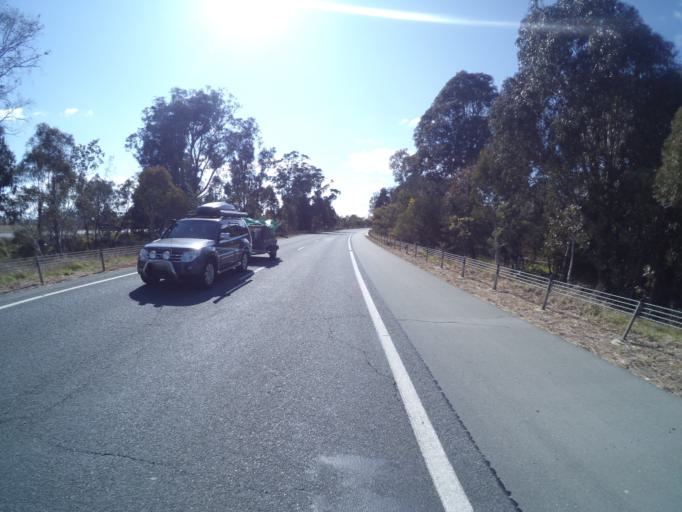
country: AU
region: Australian Capital Territory
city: Kaleen
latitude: -35.2066
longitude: 149.1959
